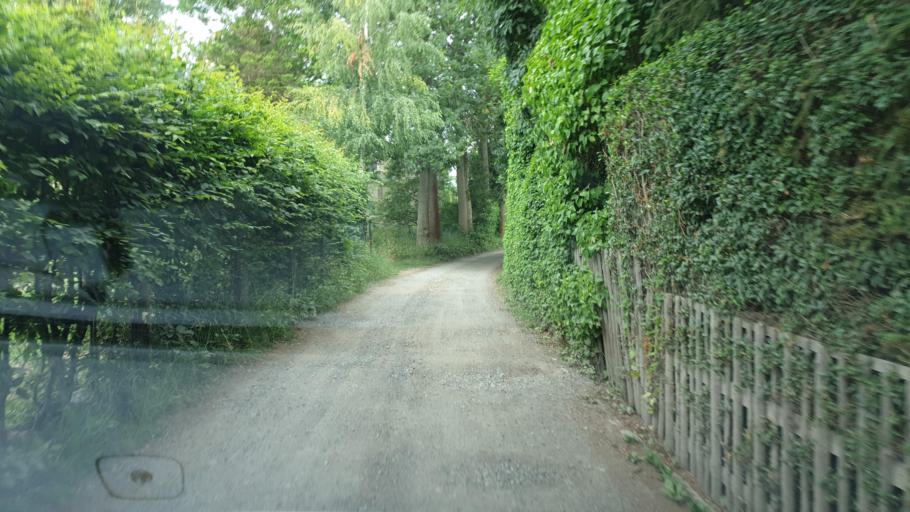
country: DE
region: Saxony
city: Stollberg
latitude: 50.7027
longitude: 12.7816
